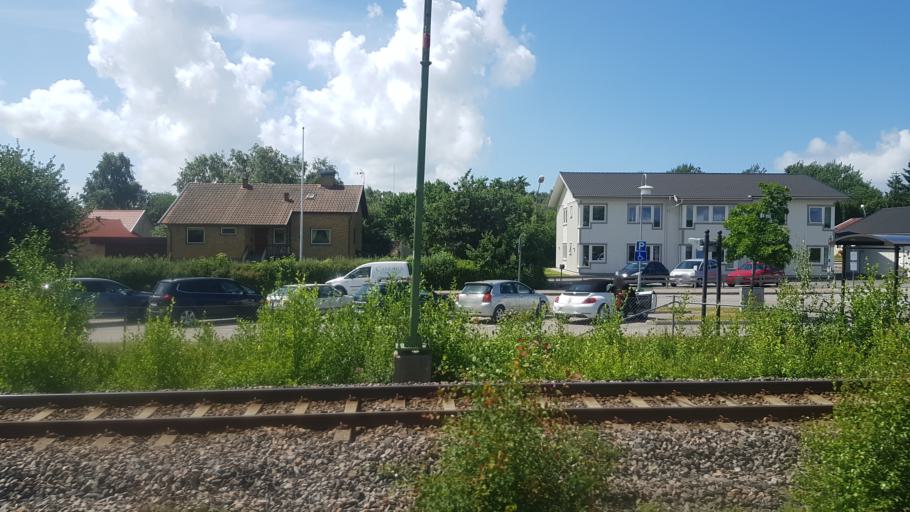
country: SE
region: Vaestra Goetaland
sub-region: Kungalvs Kommun
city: Kode
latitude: 57.9436
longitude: 11.8514
